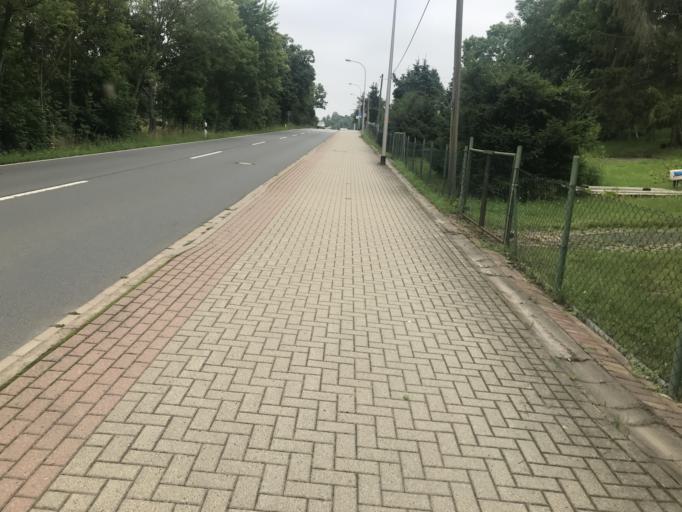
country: DE
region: Saxony-Anhalt
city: Quedlinburg
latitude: 51.7939
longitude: 11.1197
